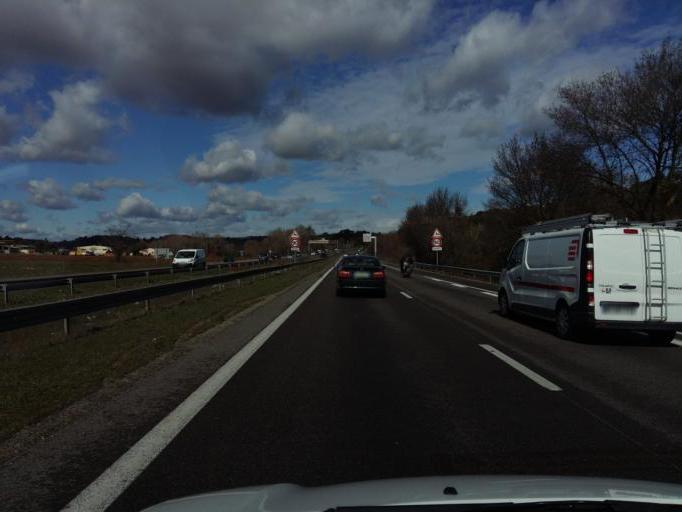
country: FR
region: Provence-Alpes-Cote d'Azur
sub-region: Departement des Bouches-du-Rhone
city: Bouc-Bel-Air
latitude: 43.4935
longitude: 5.4071
